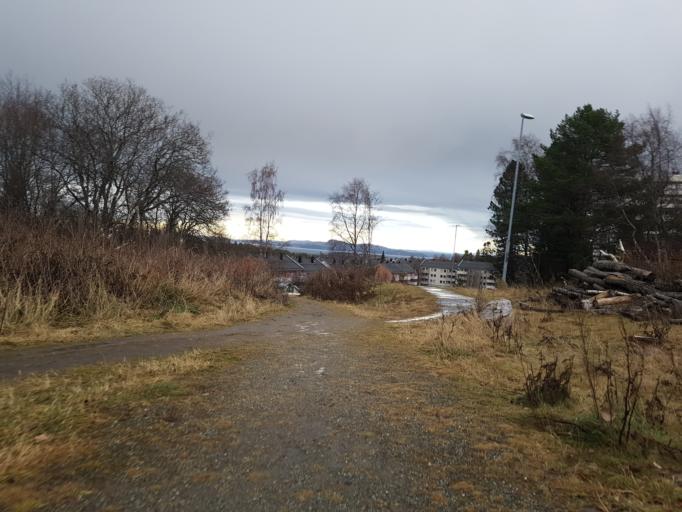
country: NO
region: Sor-Trondelag
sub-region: Trondheim
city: Trondheim
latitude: 63.4142
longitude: 10.3468
